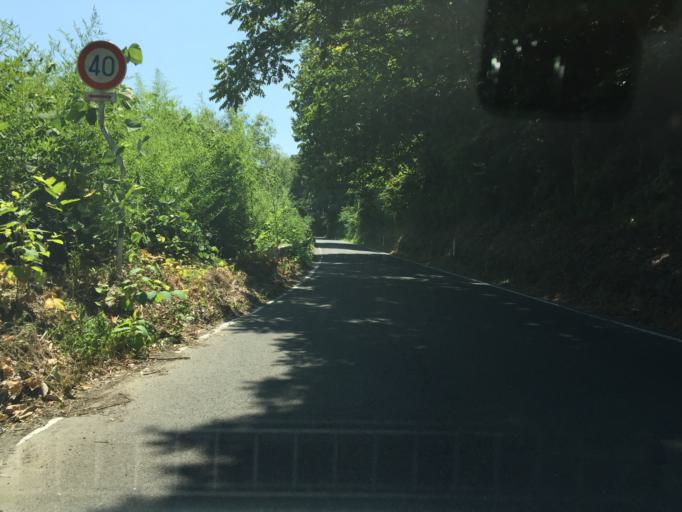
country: JP
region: Fukushima
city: Yanagawamachi-saiwaicho
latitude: 37.8981
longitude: 140.6452
